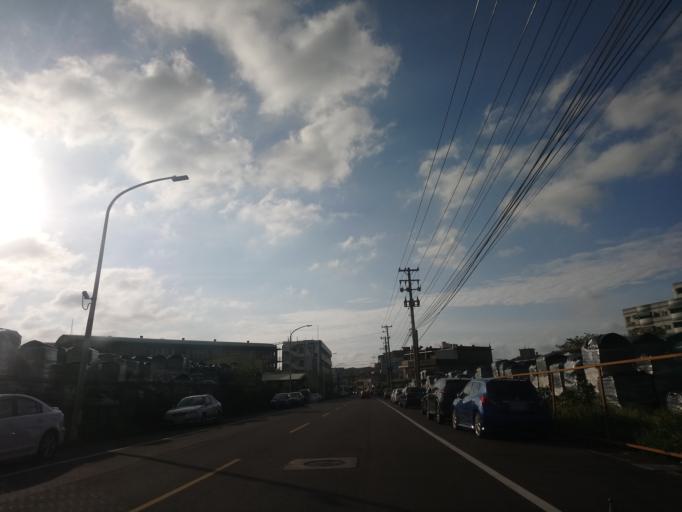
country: TW
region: Taiwan
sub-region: Hsinchu
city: Hsinchu
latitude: 24.7964
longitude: 120.9392
